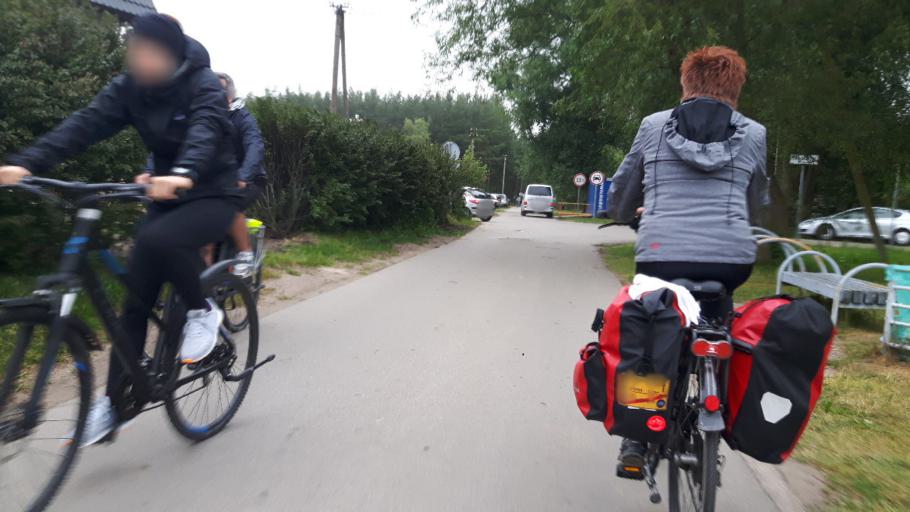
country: LT
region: Klaipedos apskritis
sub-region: Palanga
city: Sventoji
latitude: 56.0033
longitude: 21.0764
